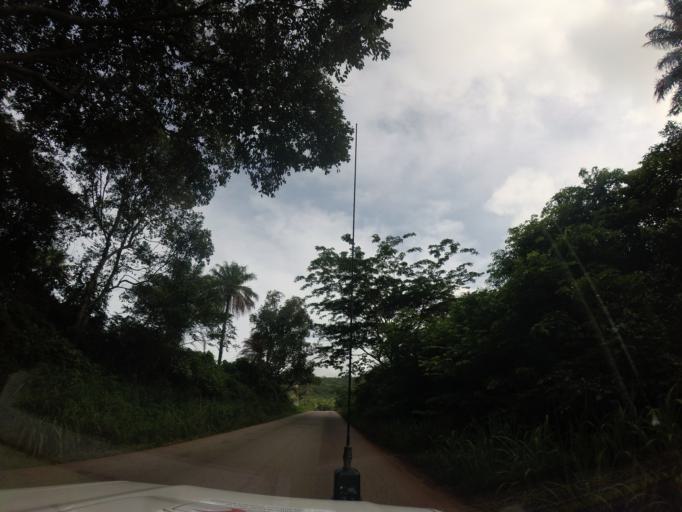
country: GN
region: Kindia
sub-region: Coyah
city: Coyah
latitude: 9.8333
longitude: -13.1250
